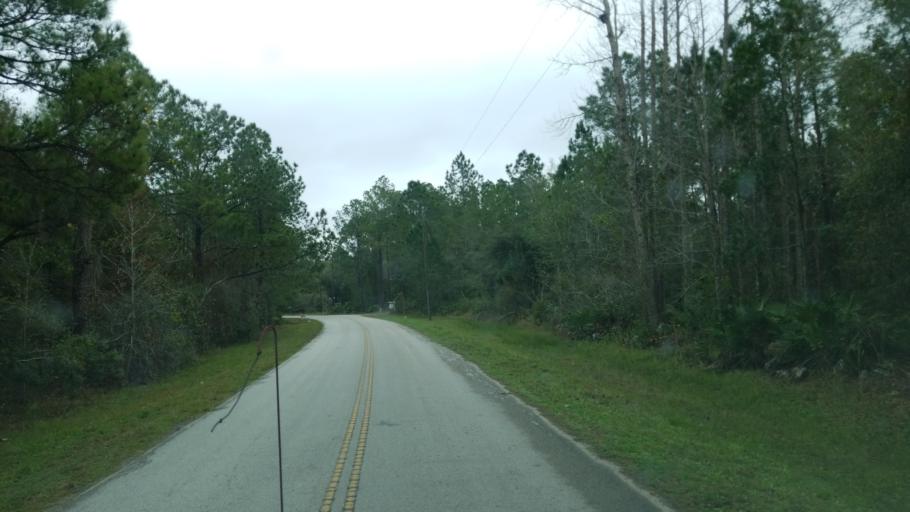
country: US
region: Florida
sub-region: Lake County
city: Groveland
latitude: 28.3828
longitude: -81.8464
